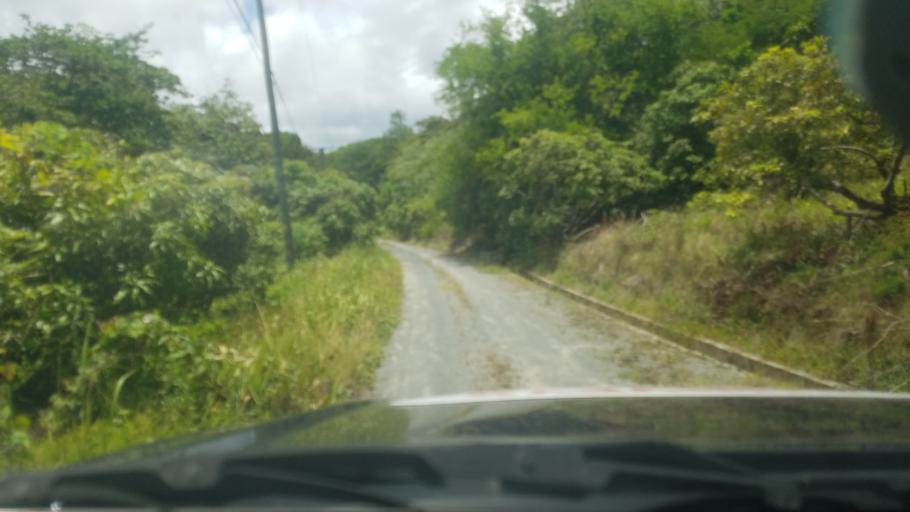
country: LC
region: Praslin
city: Praslin
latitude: 13.8662
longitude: -60.9081
